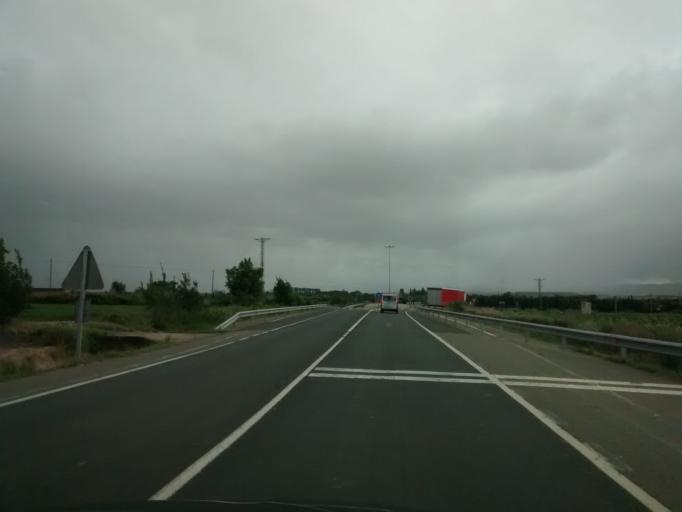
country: ES
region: Navarre
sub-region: Provincia de Navarra
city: Murchante
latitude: 42.0207
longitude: -1.6503
